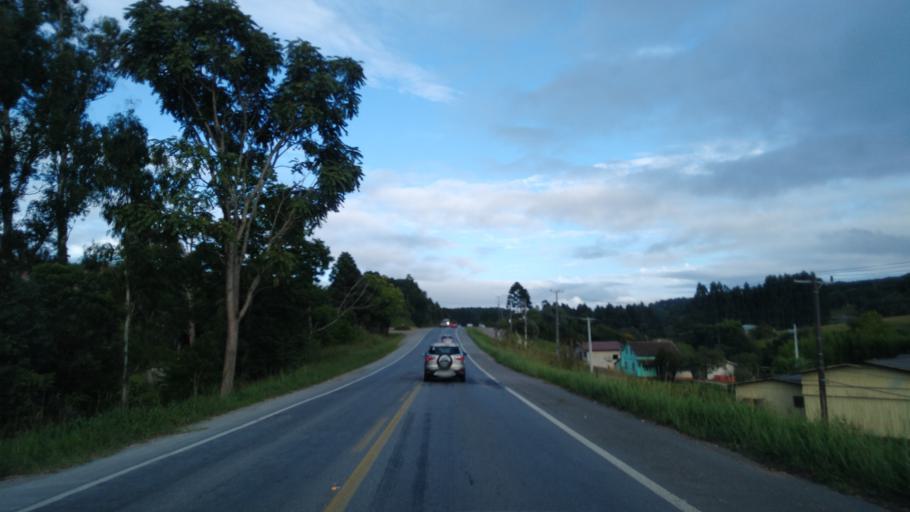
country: BR
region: Santa Catarina
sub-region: Rio Negrinho
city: Rio Negrinho
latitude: -26.2424
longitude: -49.4718
